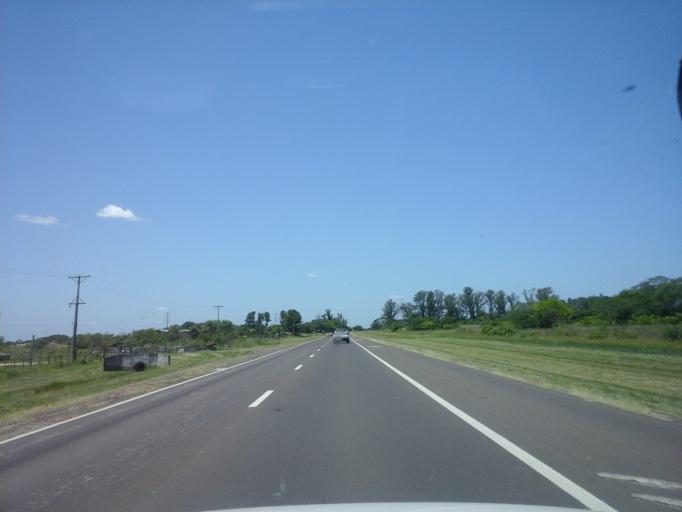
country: AR
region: Corrientes
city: Corrientes
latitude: -27.4331
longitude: -58.7312
